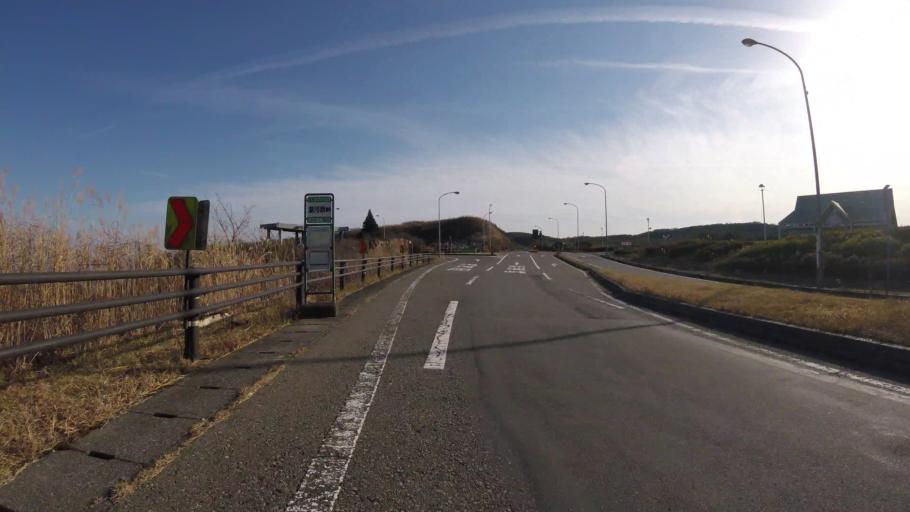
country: JP
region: Kanagawa
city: Hakone
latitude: 35.1675
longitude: 139.0286
